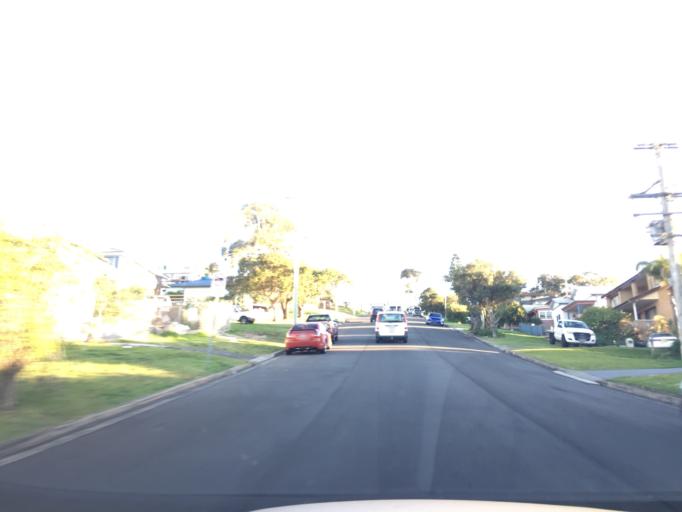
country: AU
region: New South Wales
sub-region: Kiama
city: Kiama
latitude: -34.6637
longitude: 150.8514
